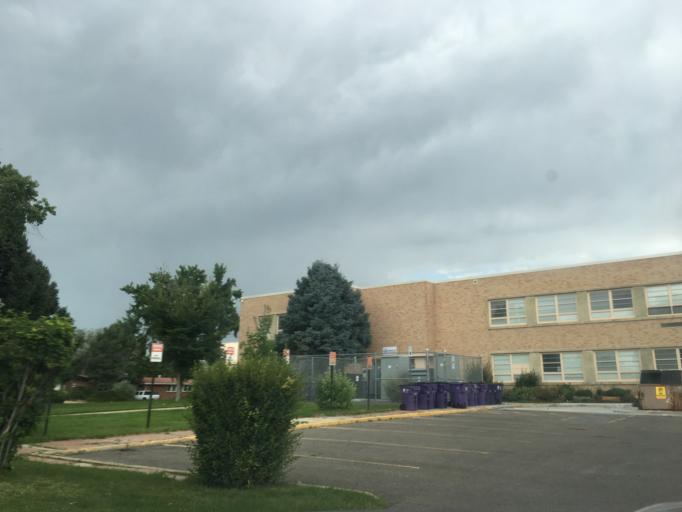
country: US
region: Colorado
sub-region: Arapahoe County
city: Sheridan
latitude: 39.6750
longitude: -105.0399
